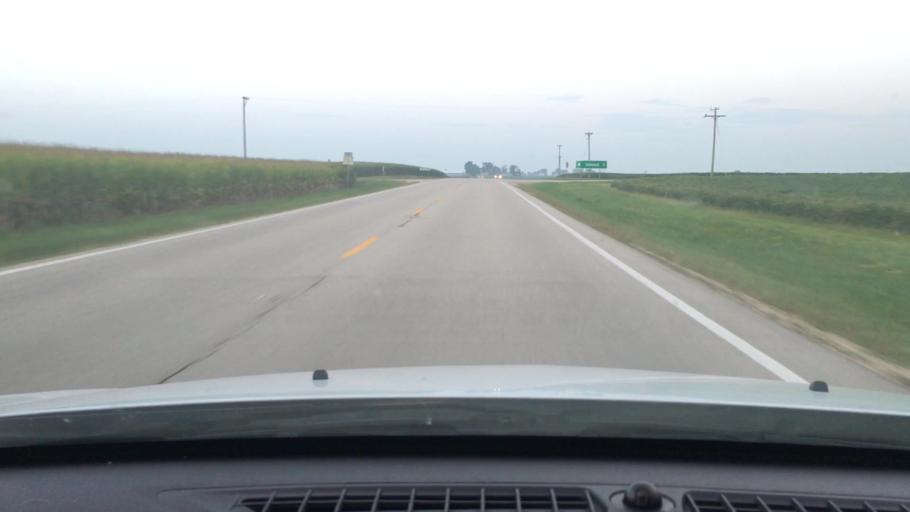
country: US
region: Illinois
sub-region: Ogle County
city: Rochelle
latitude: 41.8479
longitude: -89.0734
